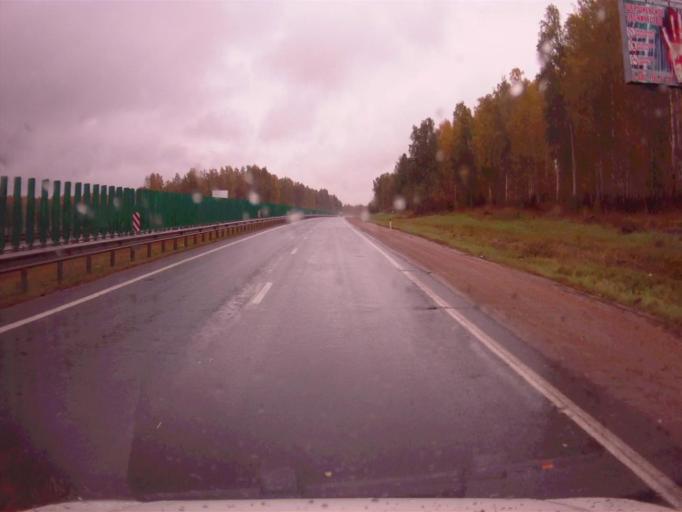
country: RU
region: Chelyabinsk
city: Dolgoderevenskoye
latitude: 55.3322
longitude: 61.3173
